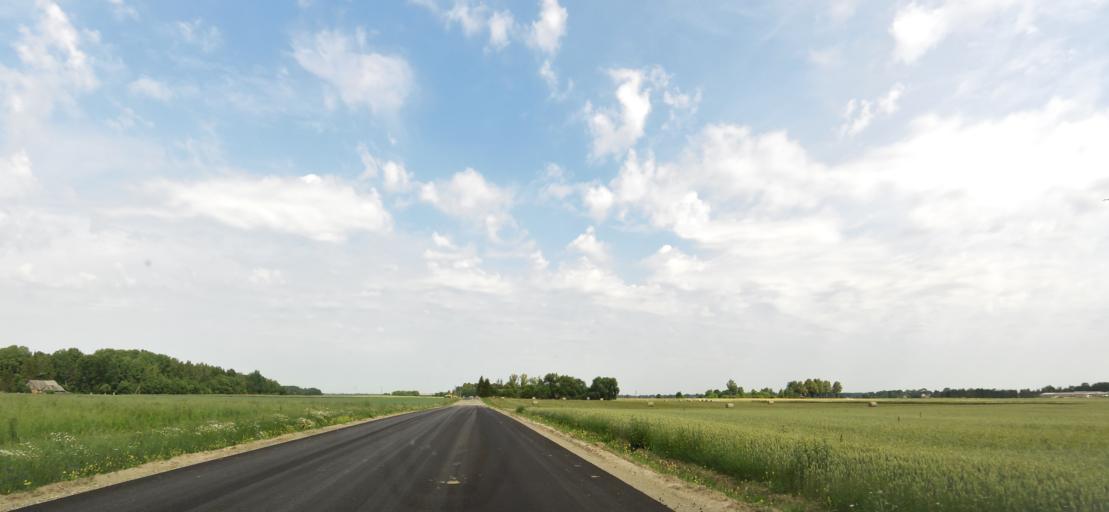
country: LT
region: Panevezys
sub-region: Birzai
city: Birzai
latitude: 56.2937
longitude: 24.6067
